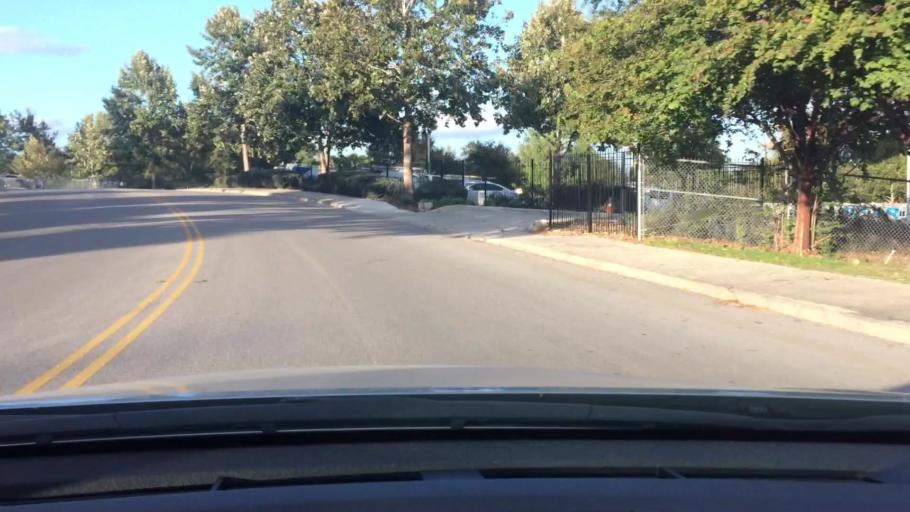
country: US
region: Texas
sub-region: Bexar County
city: Hollywood Park
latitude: 29.5517
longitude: -98.4640
